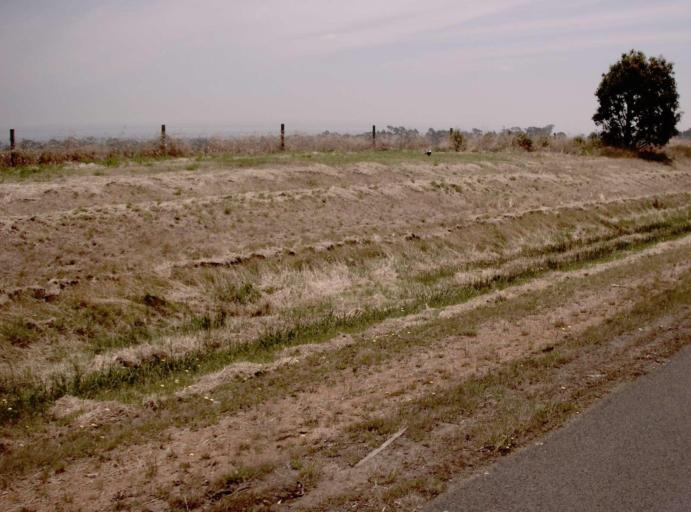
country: AU
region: Victoria
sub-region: Latrobe
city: Traralgon
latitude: -38.2455
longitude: 146.6241
